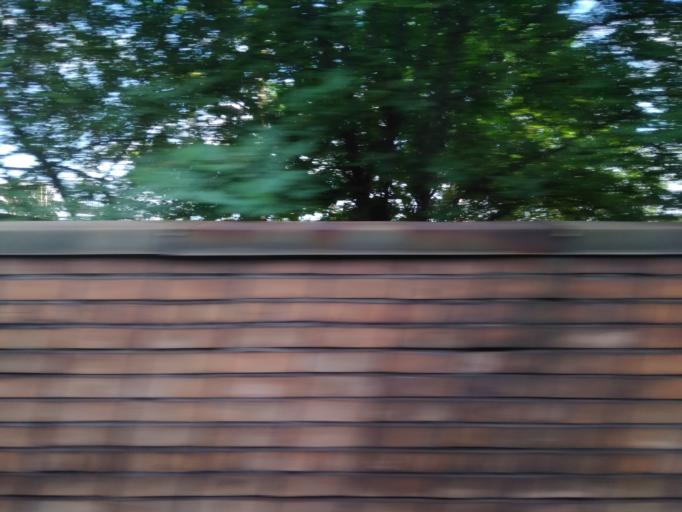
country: RU
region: Moscow
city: Sokol'niki
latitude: 55.7824
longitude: 37.6456
